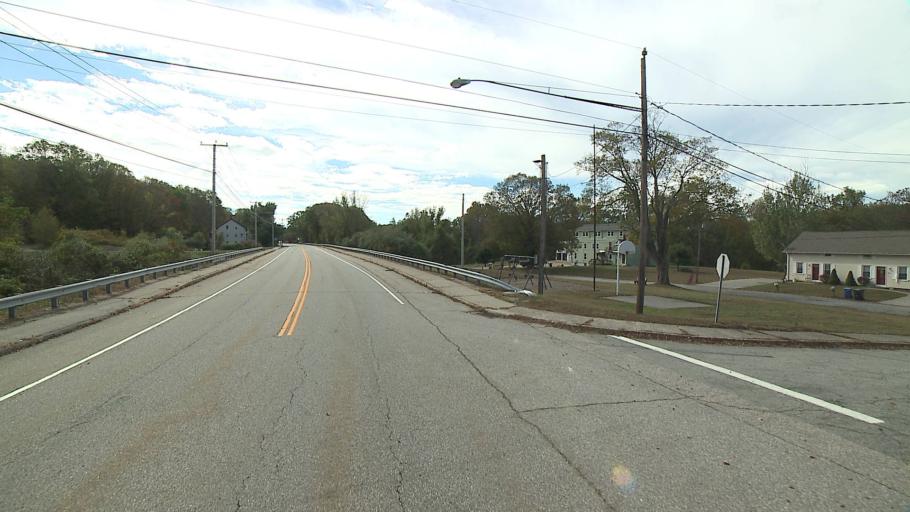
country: US
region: Connecticut
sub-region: Windham County
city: Putnam
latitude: 41.9408
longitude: -71.8940
